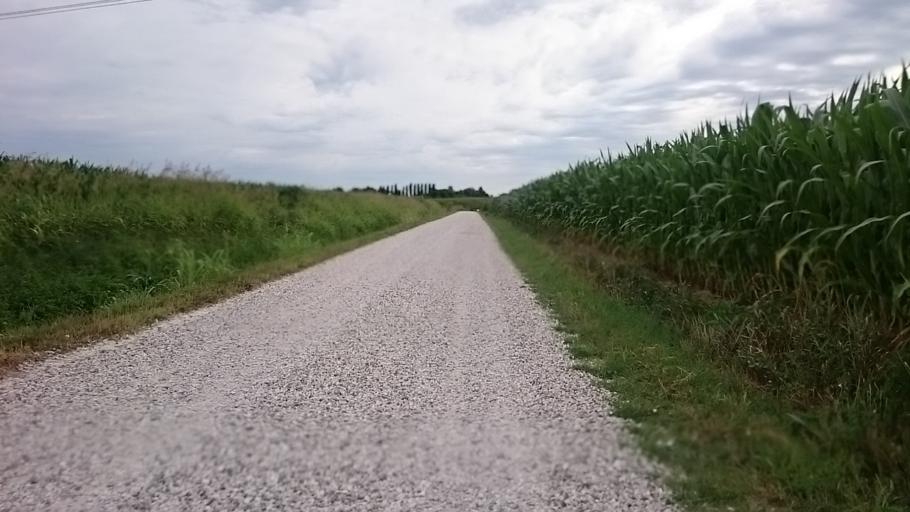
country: IT
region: Veneto
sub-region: Provincia di Padova
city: Albignasego
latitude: 45.3602
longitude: 11.8822
